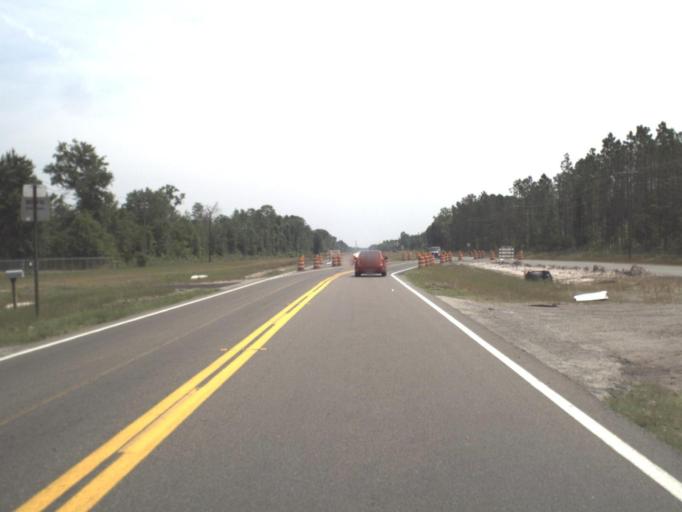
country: US
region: Florida
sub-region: Nassau County
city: Callahan
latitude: 30.5145
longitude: -81.8734
